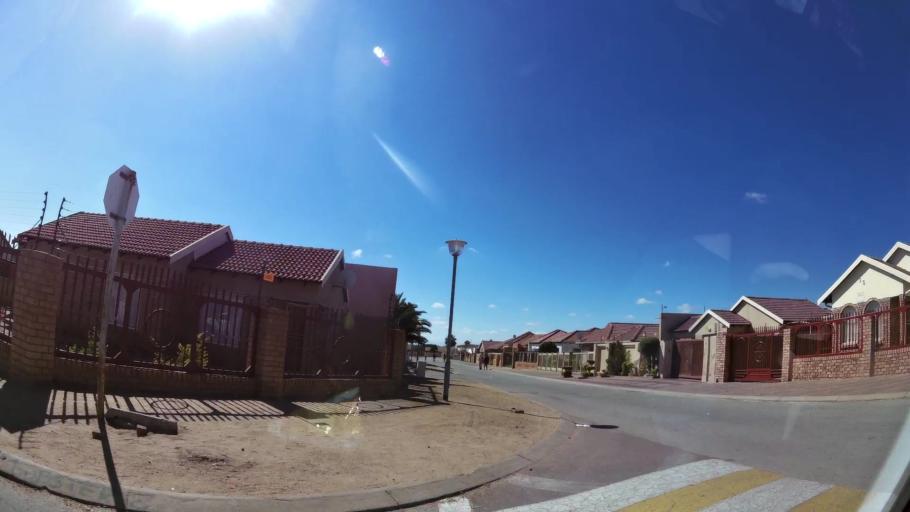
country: ZA
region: Limpopo
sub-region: Capricorn District Municipality
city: Polokwane
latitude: -23.8735
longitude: 29.4126
